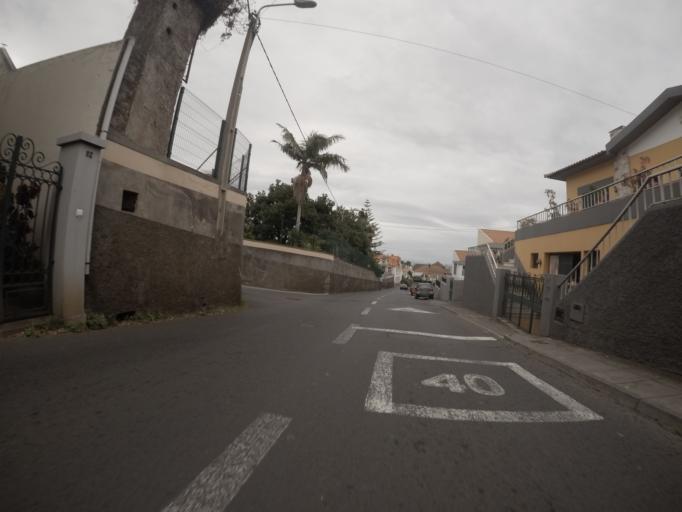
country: PT
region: Madeira
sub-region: Funchal
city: Nossa Senhora do Monte
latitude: 32.6644
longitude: -16.9310
